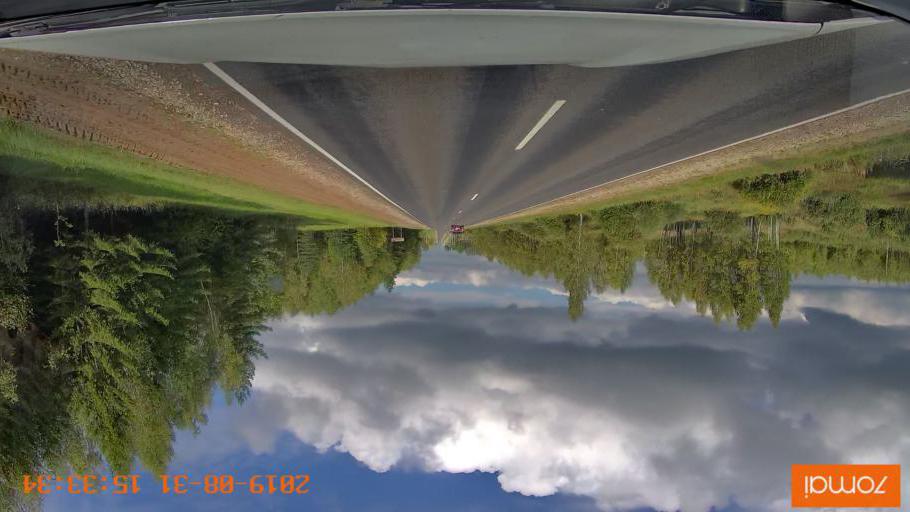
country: RU
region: Kaluga
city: Mosal'sk
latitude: 54.5958
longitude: 34.7030
